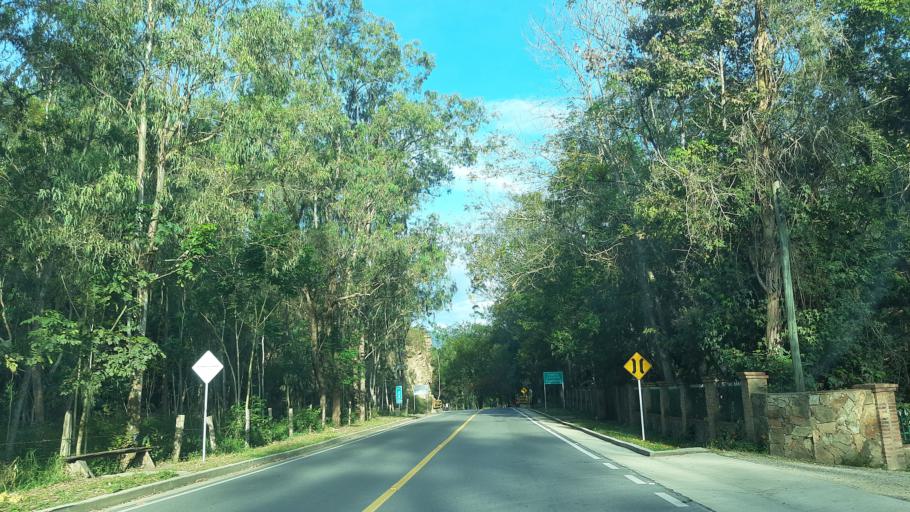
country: CO
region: Cundinamarca
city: Macheta
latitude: 5.0730
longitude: -73.5888
